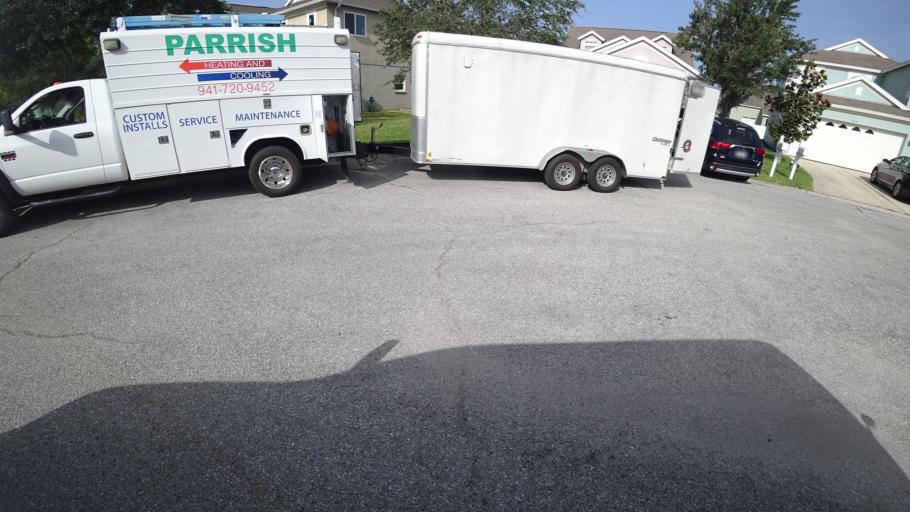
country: US
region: Florida
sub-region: Manatee County
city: Ellenton
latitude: 27.5510
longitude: -82.4957
